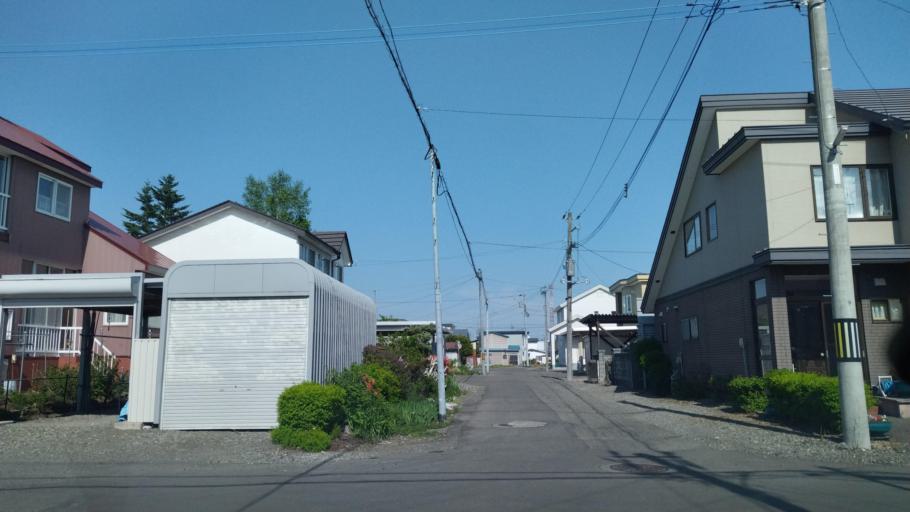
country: JP
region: Hokkaido
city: Obihiro
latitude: 42.8956
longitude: 143.1940
